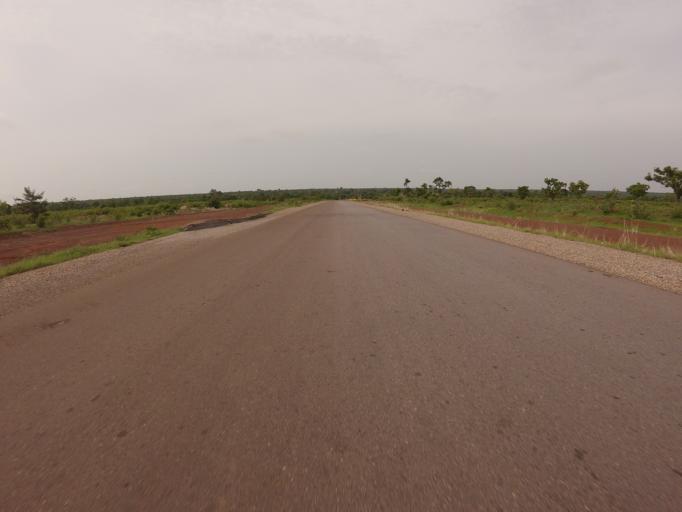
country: GH
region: Northern
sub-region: Yendi
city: Yendi
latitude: 9.7997
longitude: -0.1132
